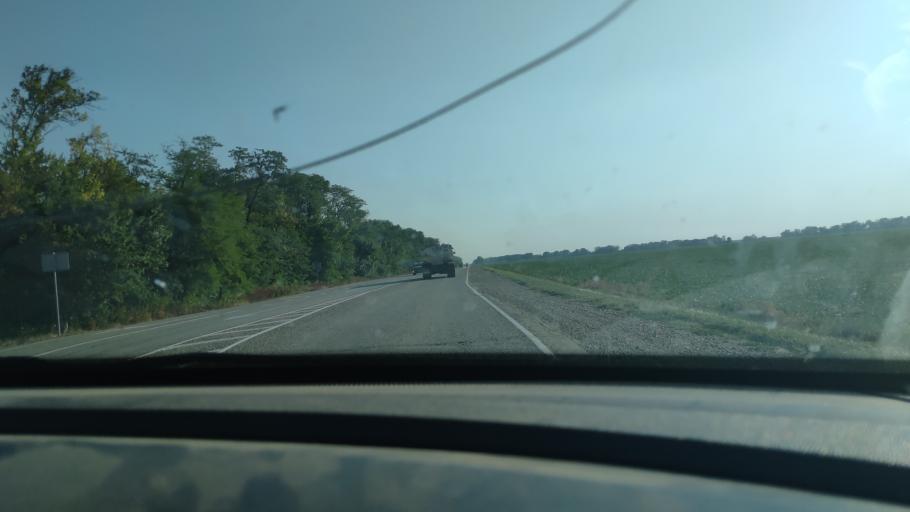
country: RU
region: Krasnodarskiy
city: Starominskaya
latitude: 46.4639
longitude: 39.0393
